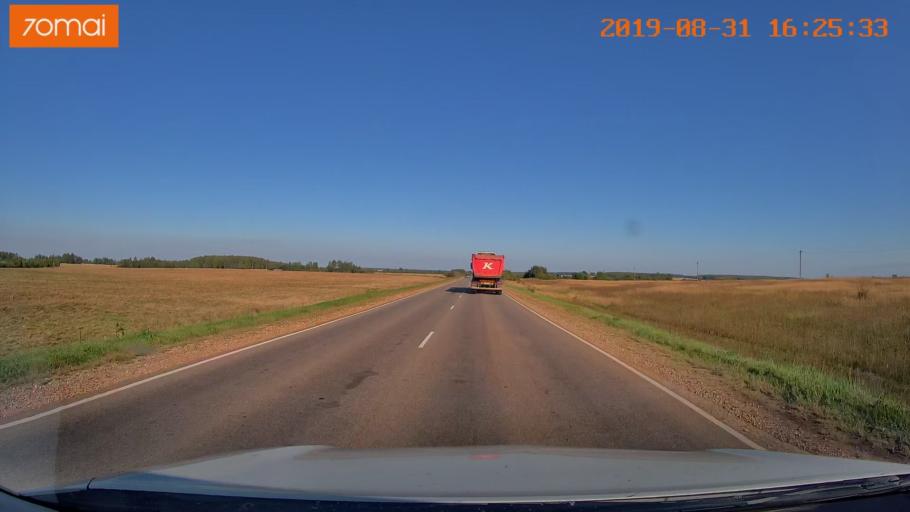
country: RU
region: Kaluga
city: Babynino
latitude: 54.5188
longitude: 35.7157
